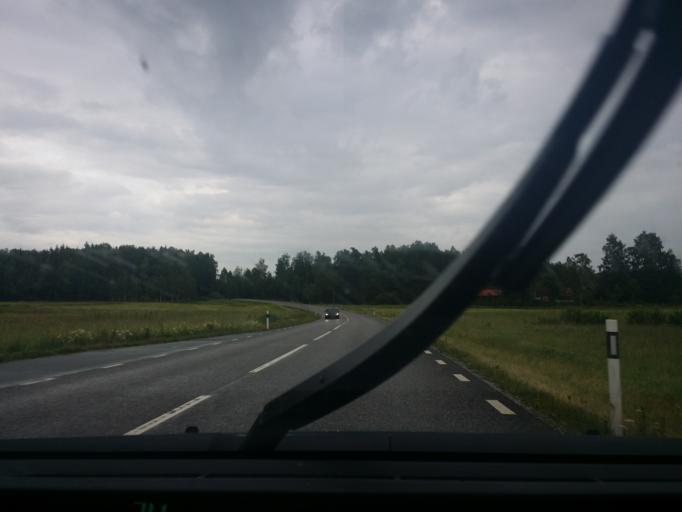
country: SE
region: OErebro
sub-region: Lindesbergs Kommun
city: Frovi
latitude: 59.4485
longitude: 15.3123
